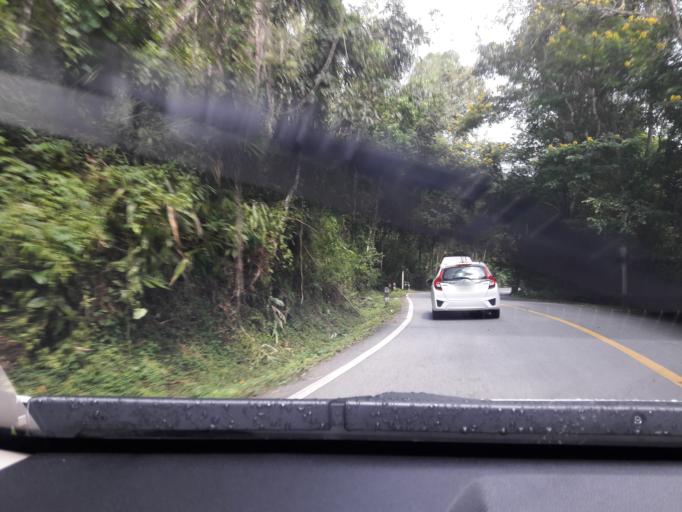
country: TH
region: Mae Hong Son
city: Mae Hi
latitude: 19.2411
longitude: 98.6554
